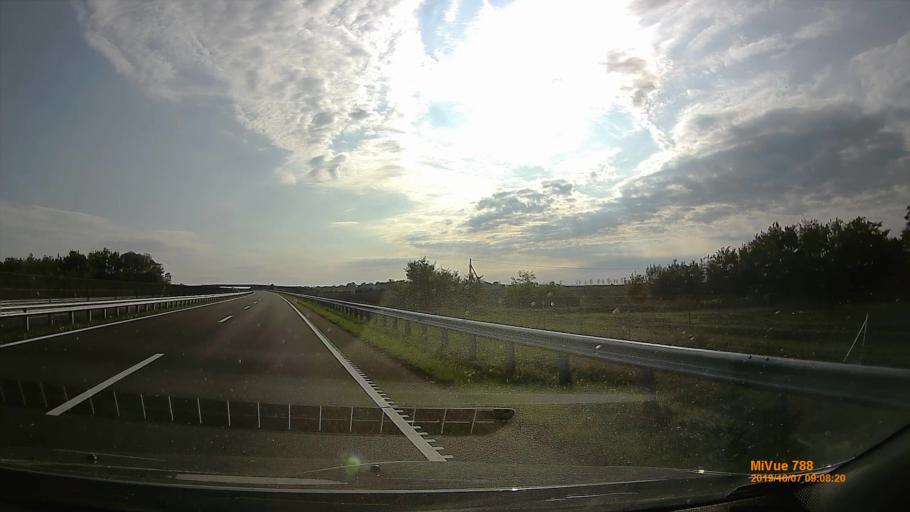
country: HU
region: Bekes
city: Szarvas
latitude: 46.8154
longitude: 20.6224
